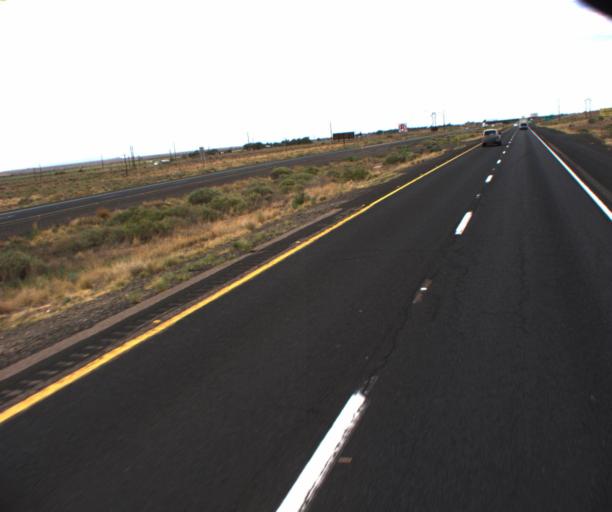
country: US
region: Arizona
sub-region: Navajo County
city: Joseph City
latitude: 34.9489
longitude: -110.3014
